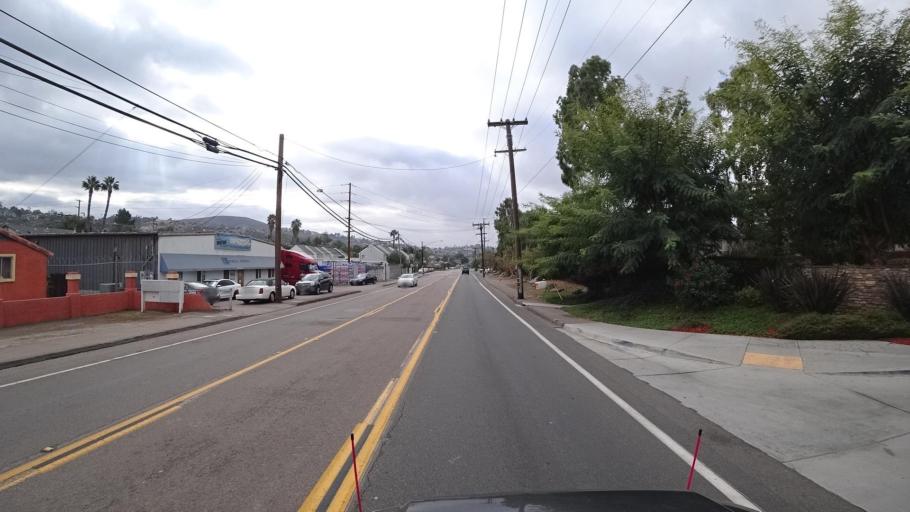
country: US
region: California
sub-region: San Diego County
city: Spring Valley
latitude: 32.7401
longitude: -117.0057
